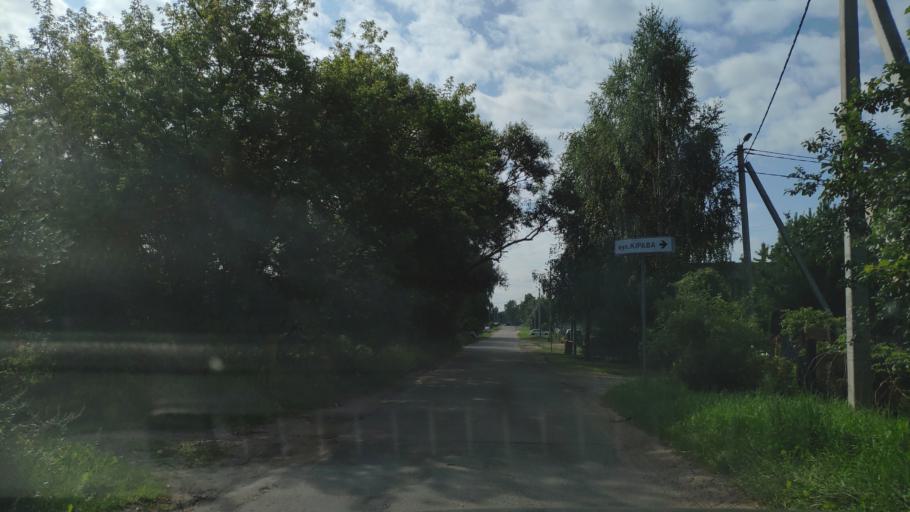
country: BY
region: Minsk
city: Zaslawye
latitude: 53.9960
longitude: 27.2820
